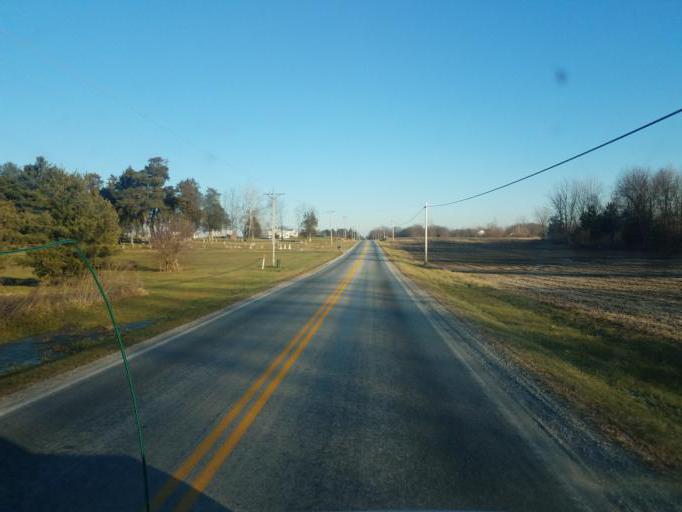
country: US
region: Ohio
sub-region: Hardin County
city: Kenton
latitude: 40.6233
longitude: -83.5131
